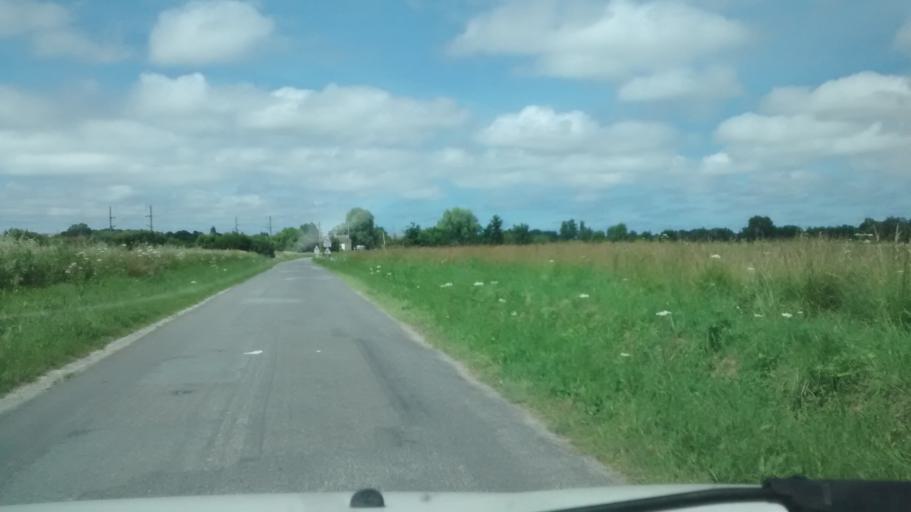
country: FR
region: Brittany
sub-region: Departement d'Ille-et-Vilaine
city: La Gouesniere
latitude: 48.6106
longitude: -1.8797
